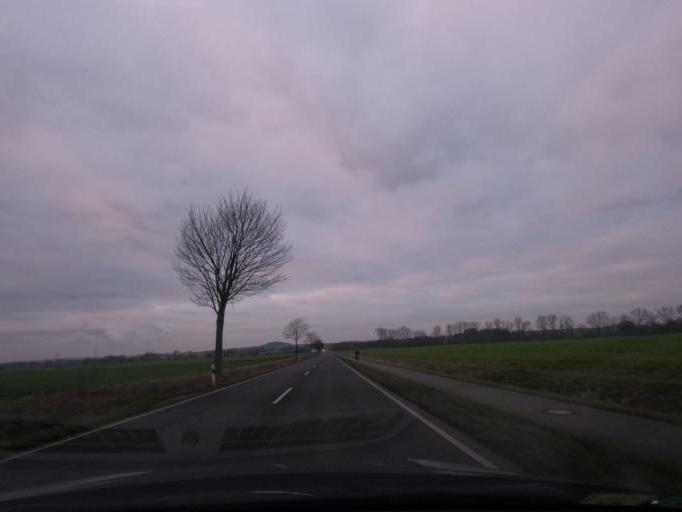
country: DE
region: Lower Saxony
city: Kissenbruck
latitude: 52.1483
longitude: 10.5998
